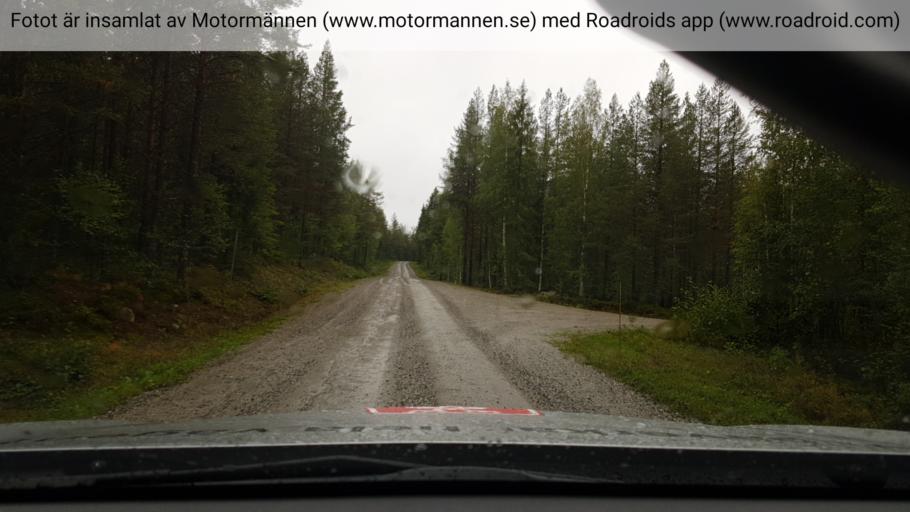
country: SE
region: Vaesterbotten
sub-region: Asele Kommun
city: Asele
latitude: 63.9947
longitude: 17.6022
